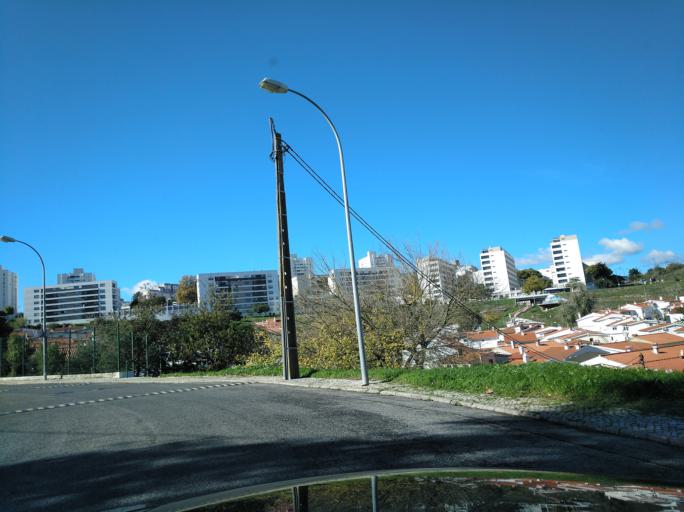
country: PT
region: Lisbon
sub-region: Loures
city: Moscavide
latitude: 38.7451
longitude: -9.1077
